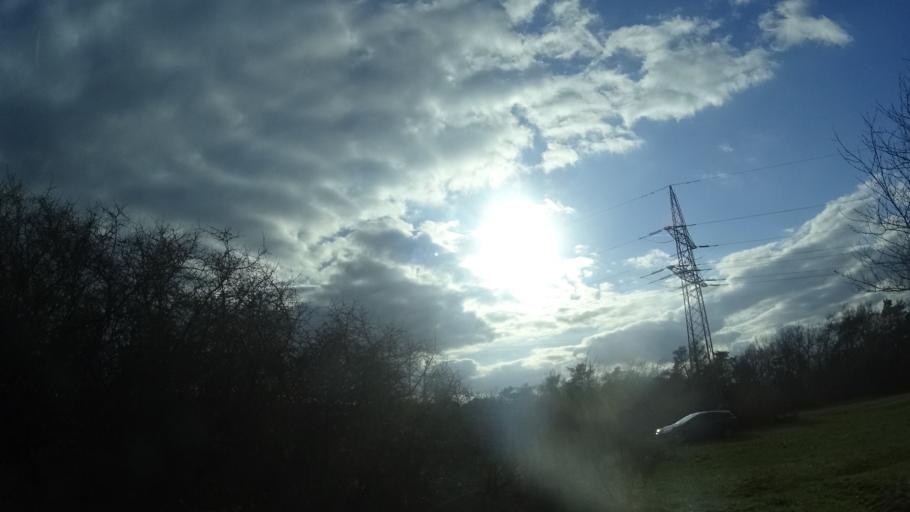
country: DE
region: Rheinland-Pfalz
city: Reichenbach
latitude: 49.6502
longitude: 7.2754
